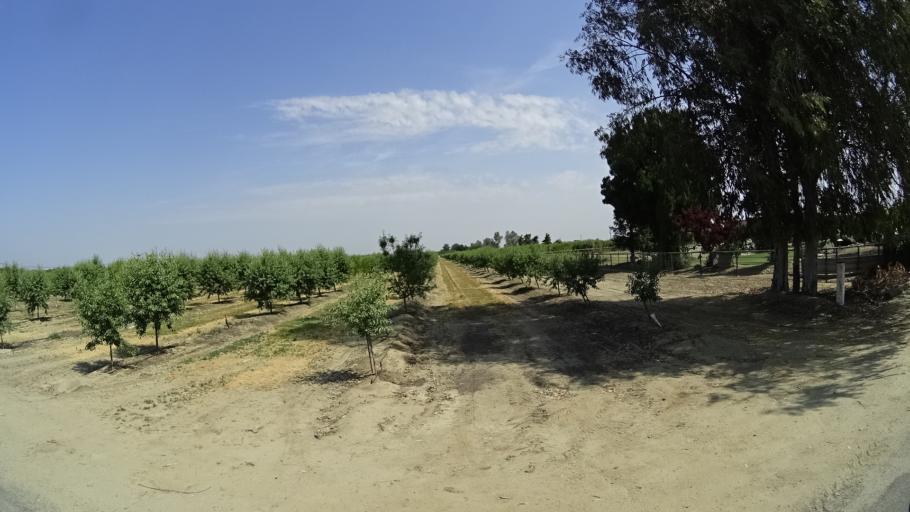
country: US
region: California
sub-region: Fresno County
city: Riverdale
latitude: 36.3948
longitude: -119.7996
